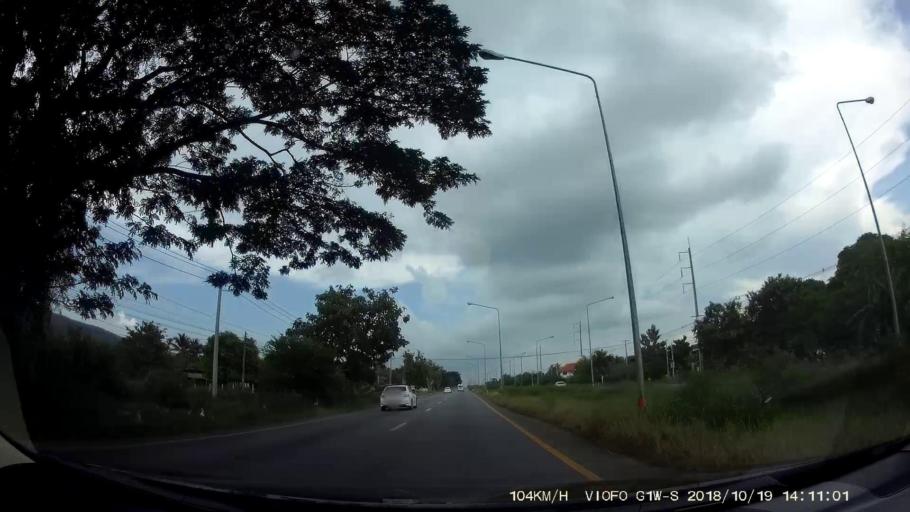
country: TH
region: Chaiyaphum
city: Khon Sawan
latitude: 15.9356
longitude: 102.1540
